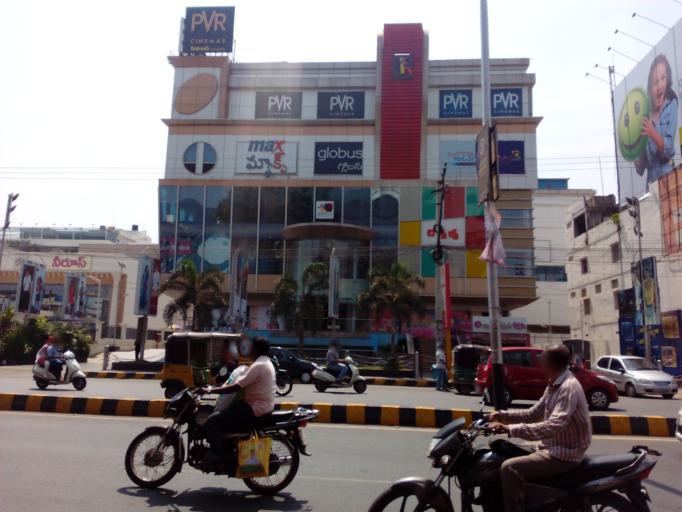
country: IN
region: Andhra Pradesh
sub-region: Krishna
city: Vijayawada
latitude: 16.5016
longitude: 80.6437
